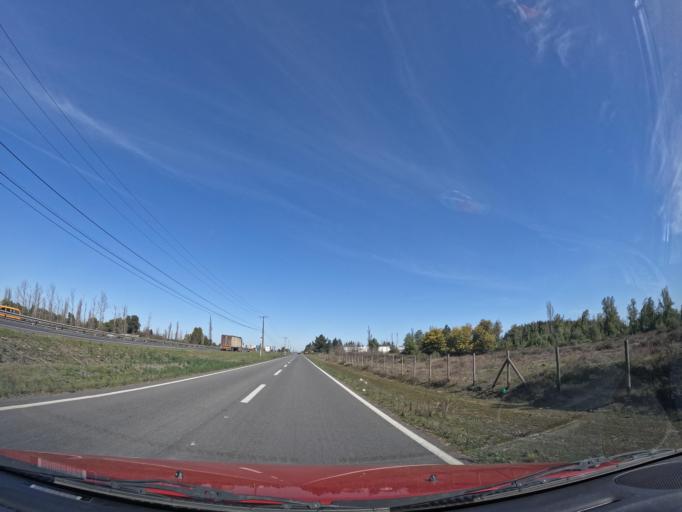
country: CL
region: Biobio
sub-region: Provincia de Biobio
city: Cabrero
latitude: -37.0241
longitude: -72.3674
